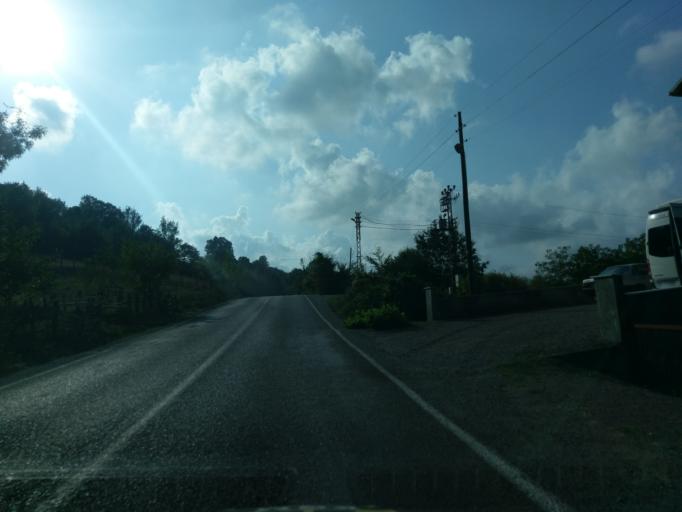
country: TR
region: Sinop
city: Helaldi
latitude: 41.8960
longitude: 34.4717
